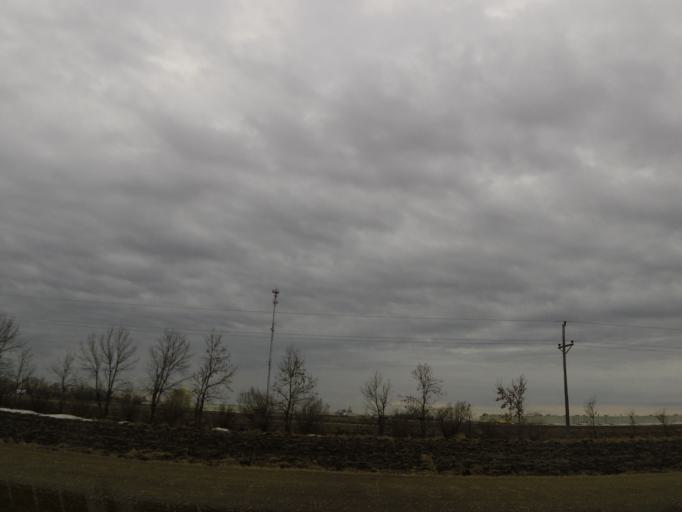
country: US
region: North Dakota
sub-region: Walsh County
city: Grafton
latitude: 48.4198
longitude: -97.4353
